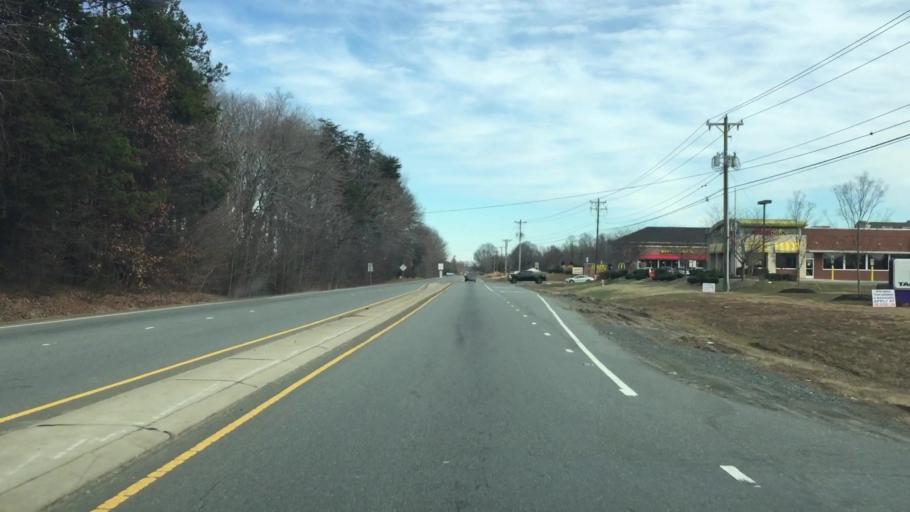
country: US
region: North Carolina
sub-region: Forsyth County
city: Walkertown
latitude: 36.1661
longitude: -80.1360
